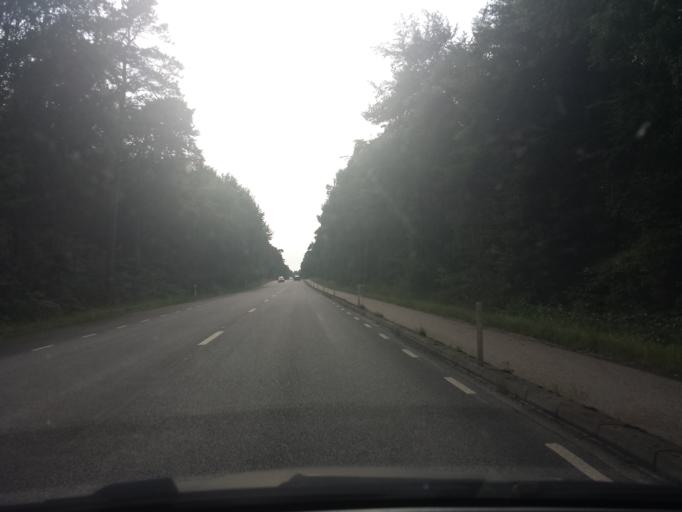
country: SE
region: Skane
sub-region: Ystads Kommun
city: Kopingebro
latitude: 55.4366
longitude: 13.9077
